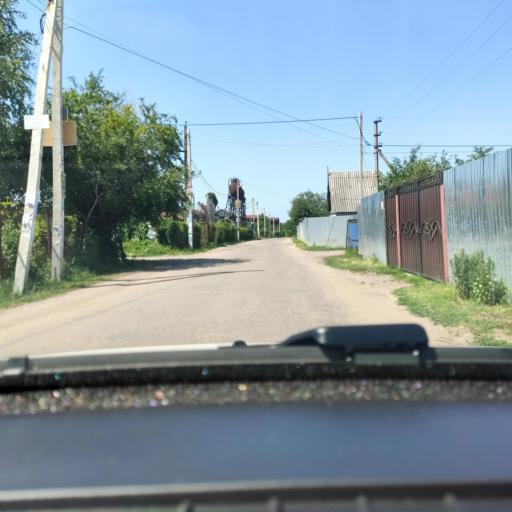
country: RU
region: Voronezj
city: Shilovo
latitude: 51.5866
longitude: 39.1569
